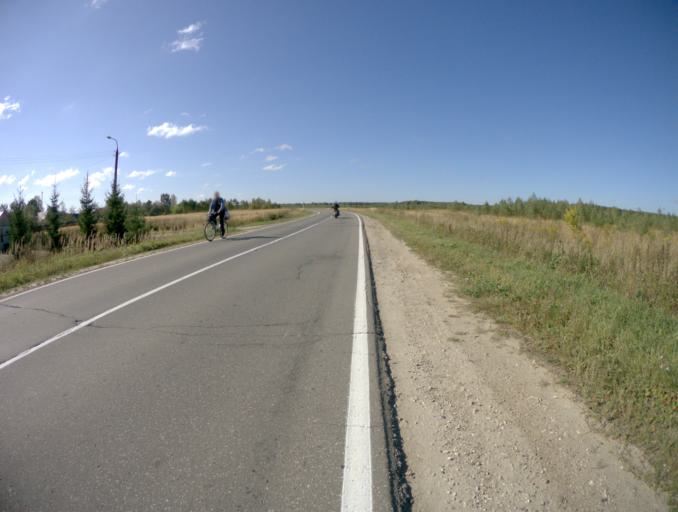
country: RU
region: Vladimir
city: Kameshkovo
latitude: 56.3525
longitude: 40.9750
